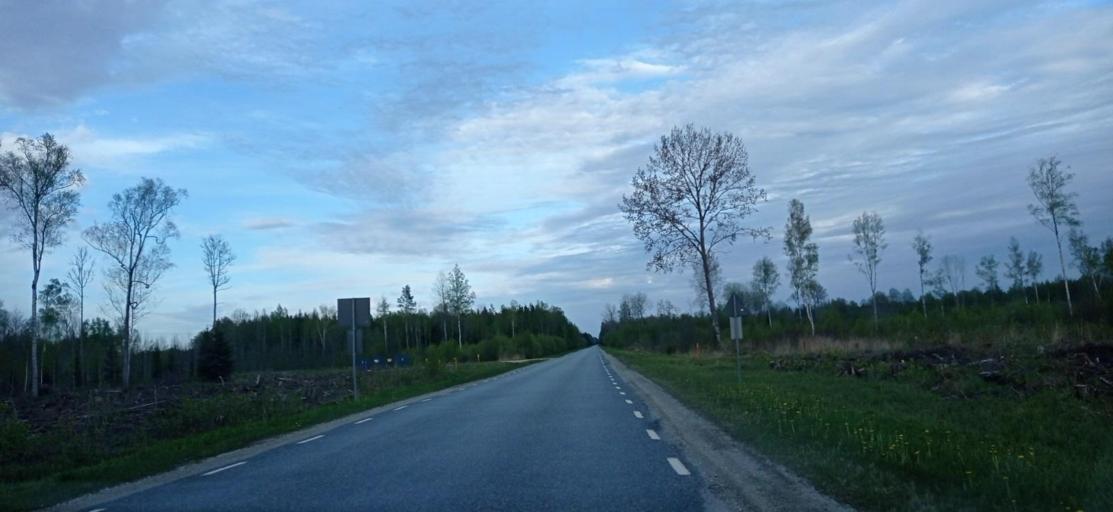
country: EE
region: Paernumaa
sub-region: Tootsi vald
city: Tootsi
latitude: 58.5672
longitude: 24.8137
